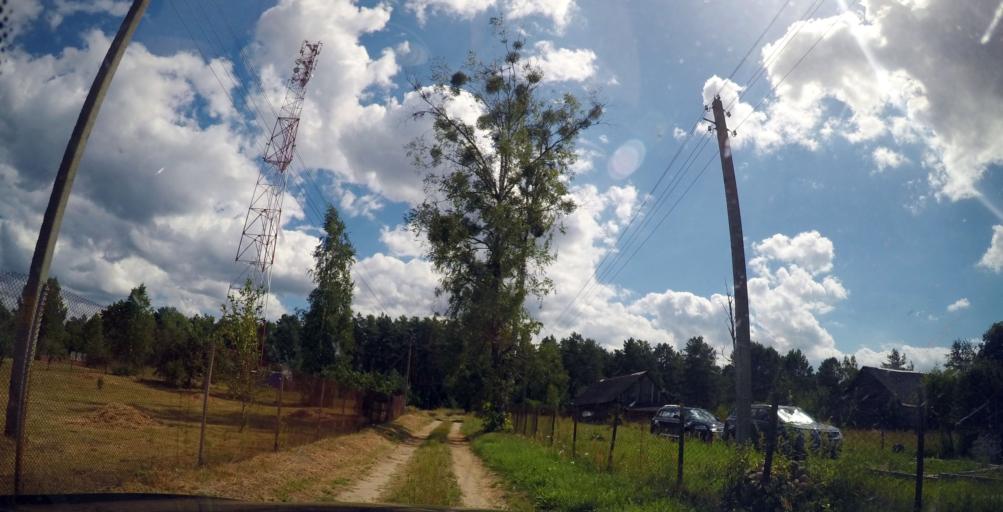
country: BY
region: Grodnenskaya
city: Skidal'
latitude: 53.8198
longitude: 24.2467
